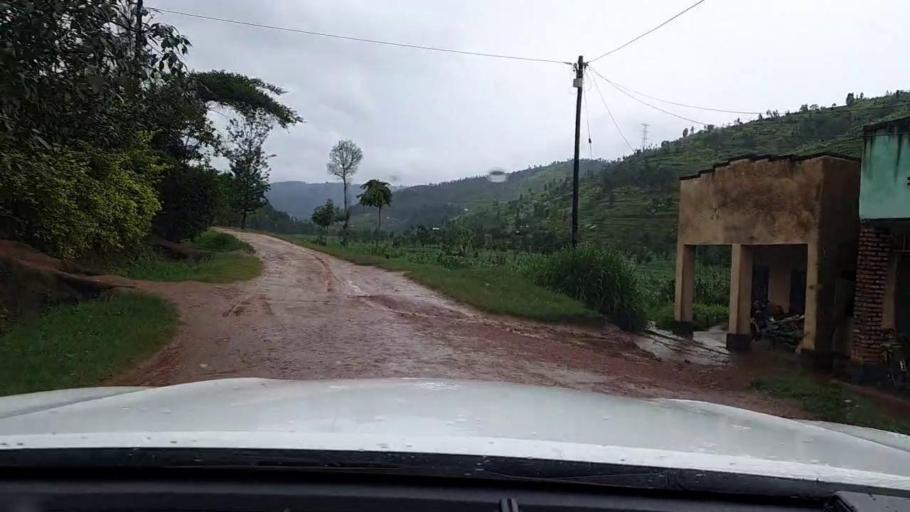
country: RW
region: Northern Province
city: Byumba
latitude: -1.7424
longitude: 29.9447
